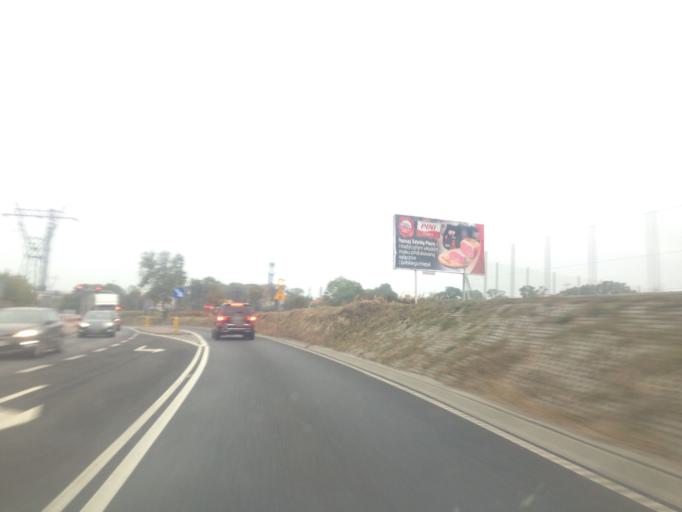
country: PL
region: Greater Poland Voivodeship
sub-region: Powiat gnieznienski
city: Trzemeszno
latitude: 52.5681
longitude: 17.8253
